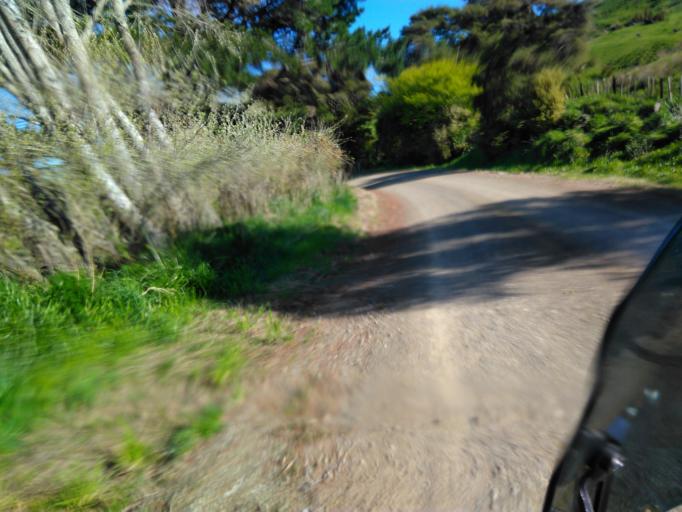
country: NZ
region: Gisborne
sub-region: Gisborne District
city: Gisborne
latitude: -38.4164
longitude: 177.6957
